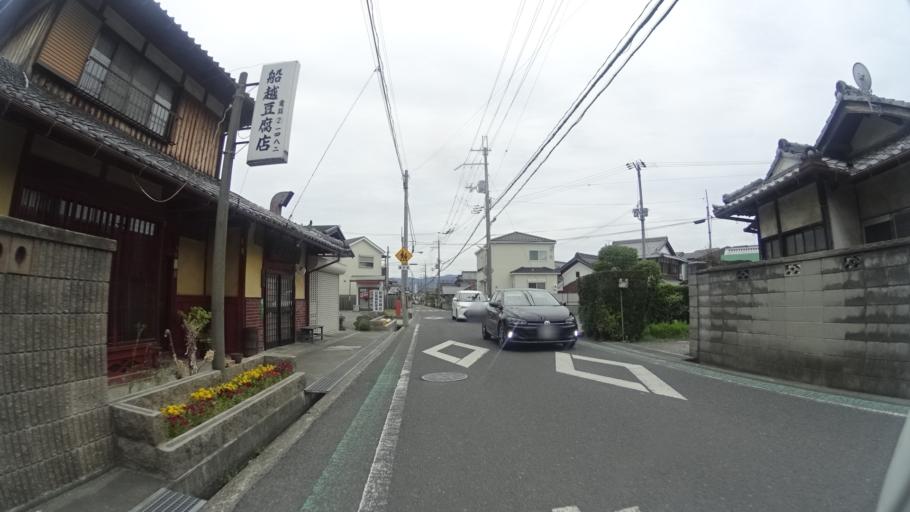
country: JP
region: Kyoto
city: Kameoka
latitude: 35.0303
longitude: 135.5568
